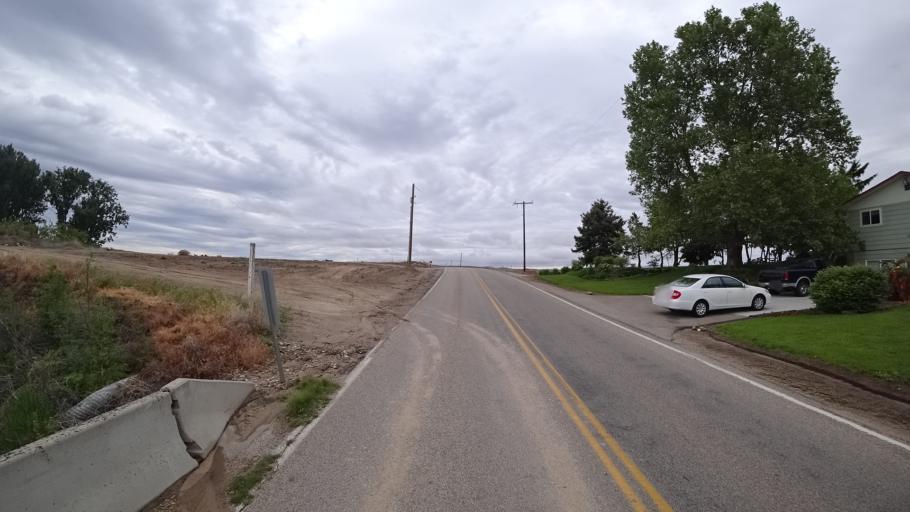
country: US
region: Idaho
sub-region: Ada County
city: Star
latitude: 43.7082
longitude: -116.4434
